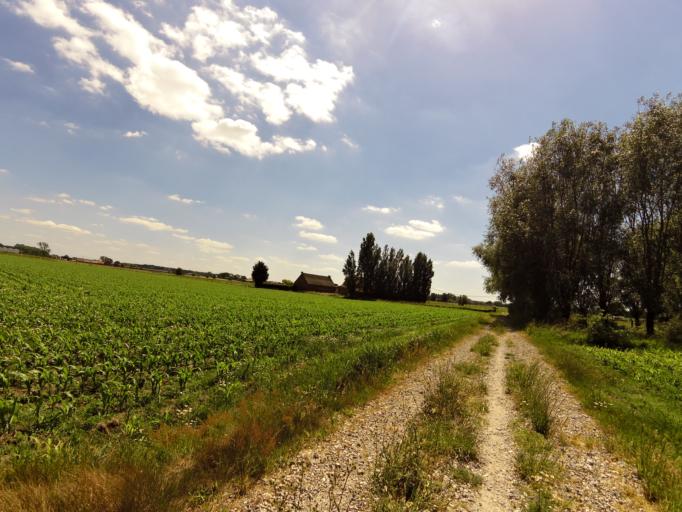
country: BE
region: Flanders
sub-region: Provincie West-Vlaanderen
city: Zedelgem
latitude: 51.1407
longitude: 3.0993
